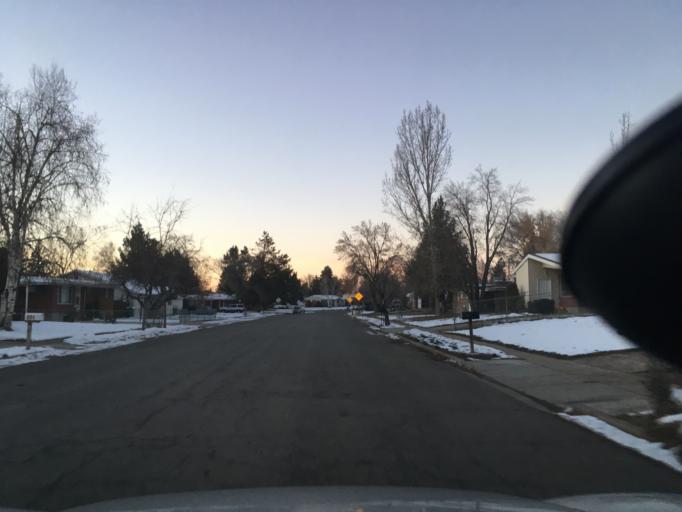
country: US
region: Utah
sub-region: Davis County
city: Layton
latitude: 41.0634
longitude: -111.9639
